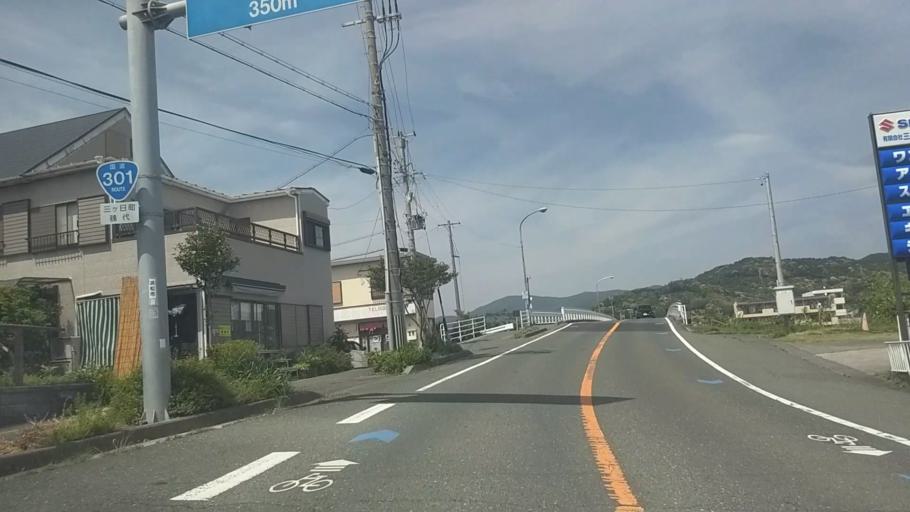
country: JP
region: Shizuoka
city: Kosai-shi
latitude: 34.8004
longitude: 137.5486
